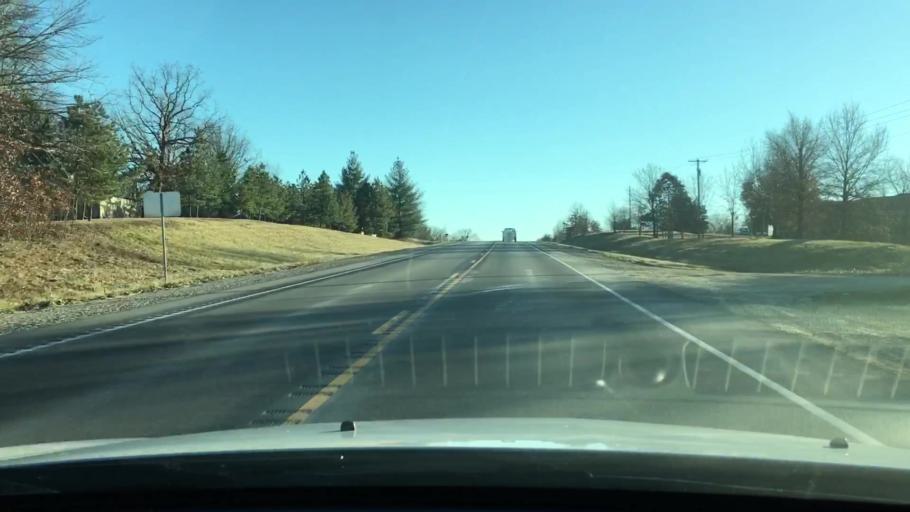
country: US
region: Missouri
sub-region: Boone County
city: Centralia
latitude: 39.1728
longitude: -92.1775
